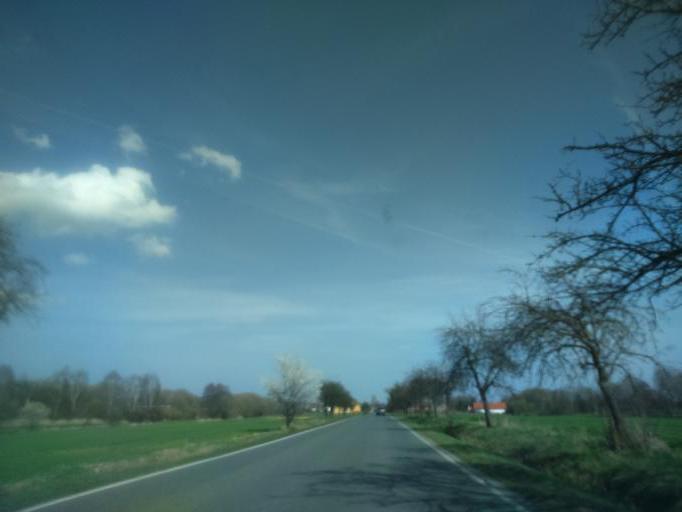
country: CZ
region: Plzensky
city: Hermanova Hut'
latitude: 49.7053
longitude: 13.0923
